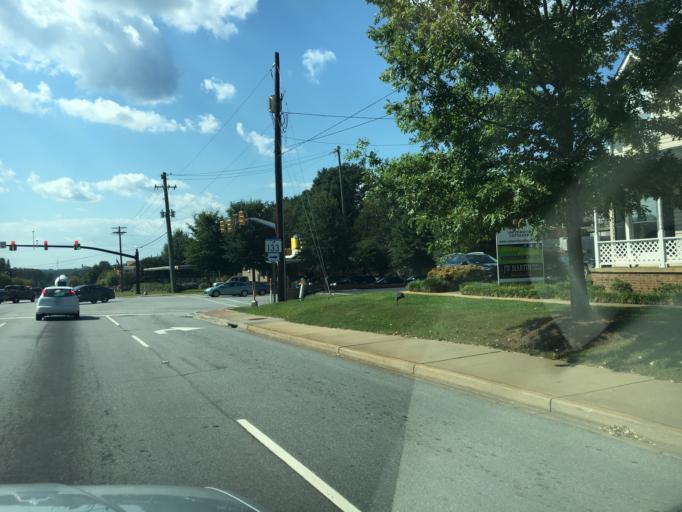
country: US
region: South Carolina
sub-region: Pickens County
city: Clemson
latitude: 34.6909
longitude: -82.8331
